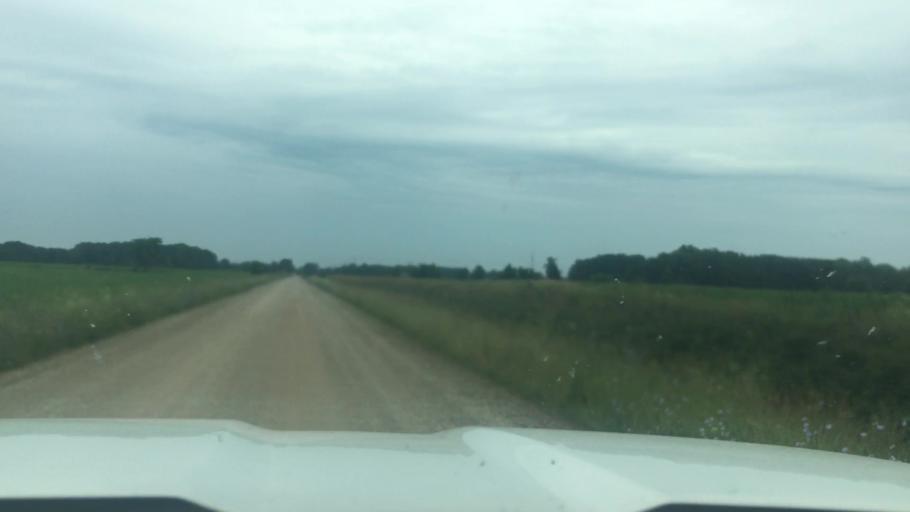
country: US
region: Michigan
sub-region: Clinton County
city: Saint Johns
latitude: 43.0775
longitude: -84.4840
